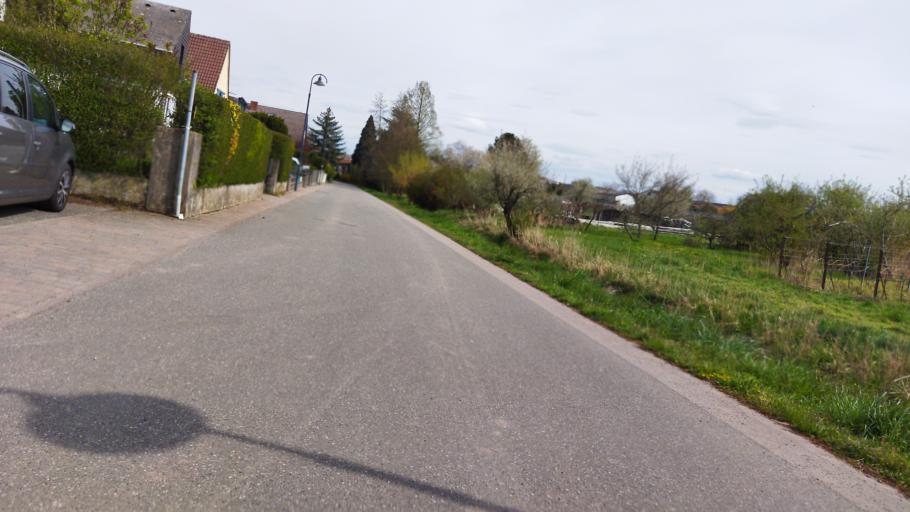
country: DE
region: Rheinland-Pfalz
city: Hainfeld
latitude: 49.2570
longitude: 8.0947
